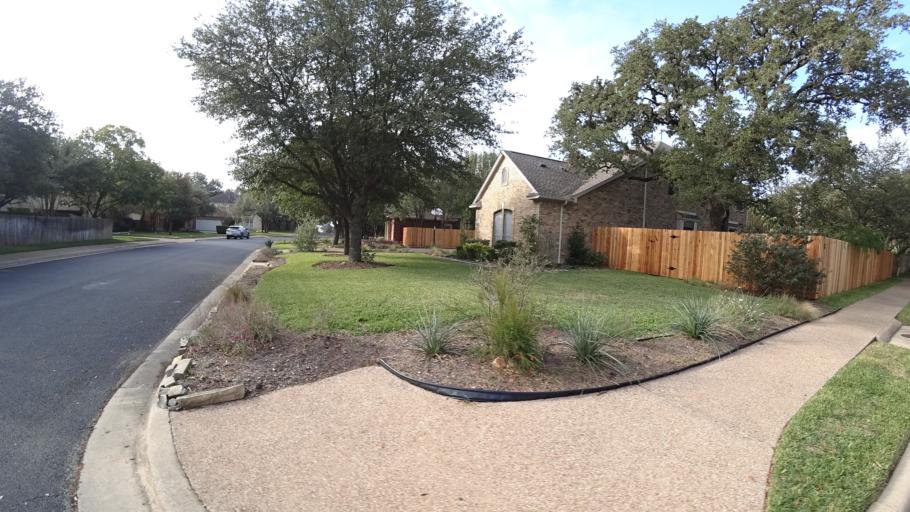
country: US
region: Texas
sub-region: Travis County
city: Shady Hollow
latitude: 30.1942
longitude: -97.8798
